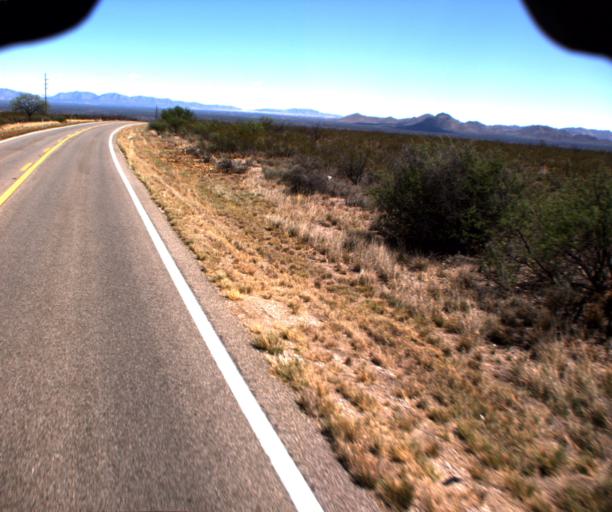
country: US
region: Arizona
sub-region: Cochise County
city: Huachuca City
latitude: 31.7187
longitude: -110.2420
